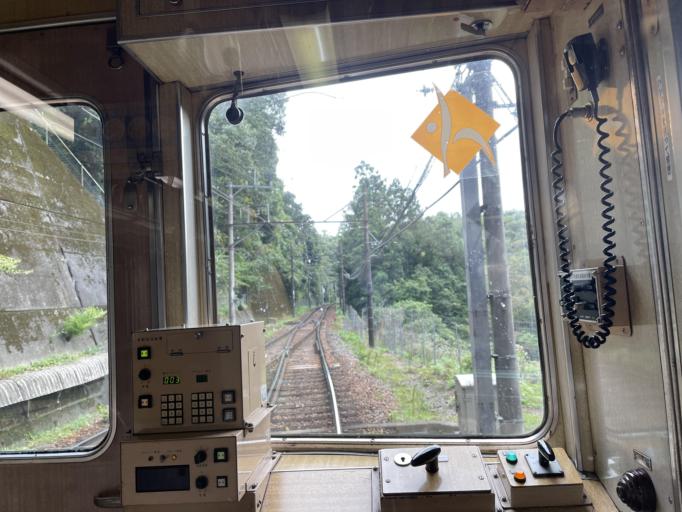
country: JP
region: Osaka
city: Ikeda
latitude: 34.8980
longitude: 135.4295
